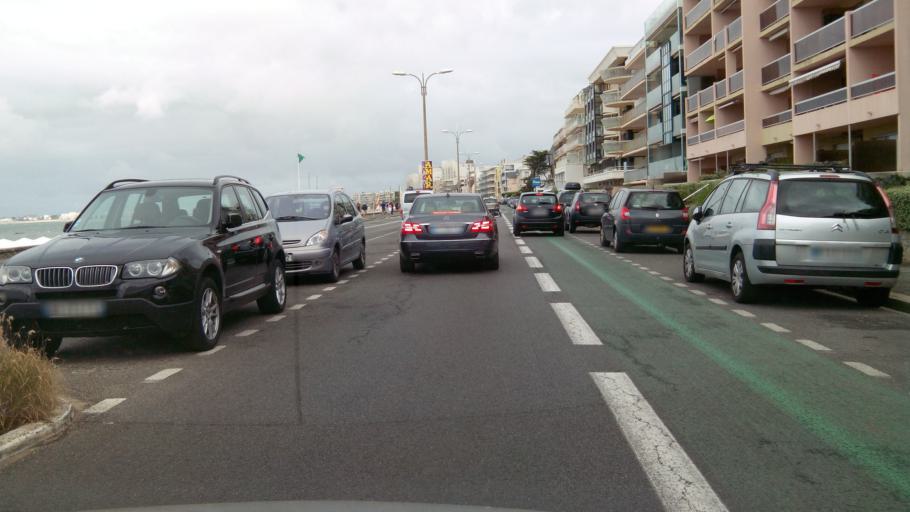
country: FR
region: Pays de la Loire
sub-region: Departement de la Loire-Atlantique
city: Pornichet
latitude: 47.2697
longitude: -2.3510
